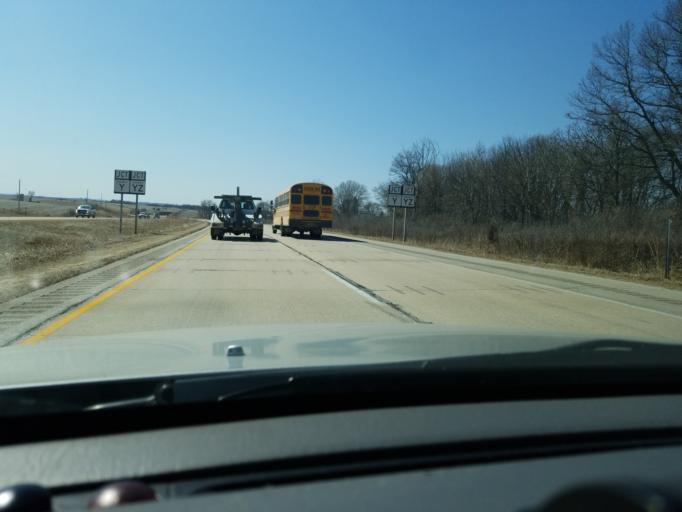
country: US
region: Wisconsin
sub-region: Iowa County
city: Dodgeville
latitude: 42.9725
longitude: -90.0399
